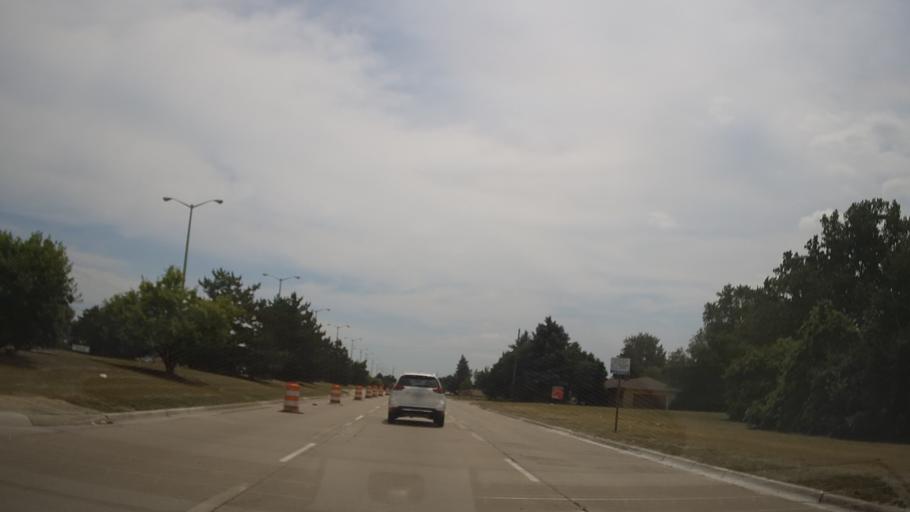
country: US
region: Michigan
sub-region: Macomb County
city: Utica
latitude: 42.6060
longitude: -83.0514
